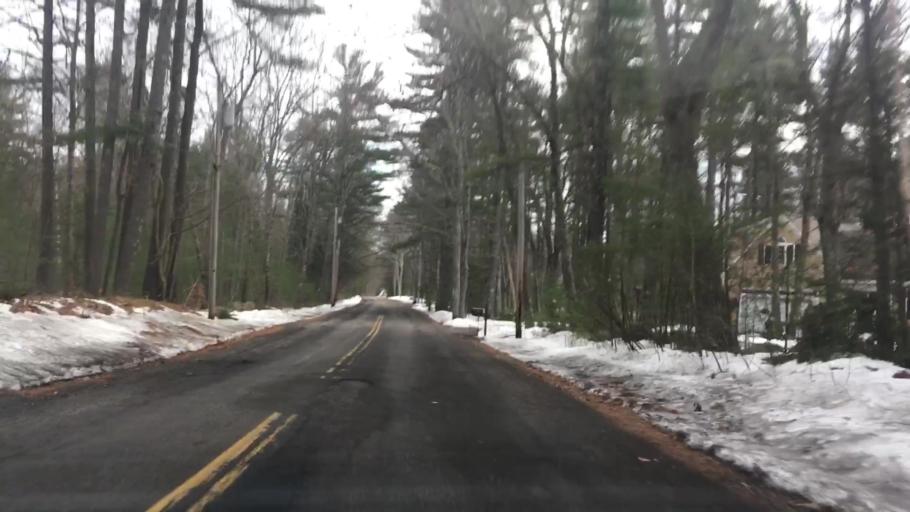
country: US
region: Maine
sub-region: York County
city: Wells Beach Station
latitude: 43.3424
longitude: -70.6133
